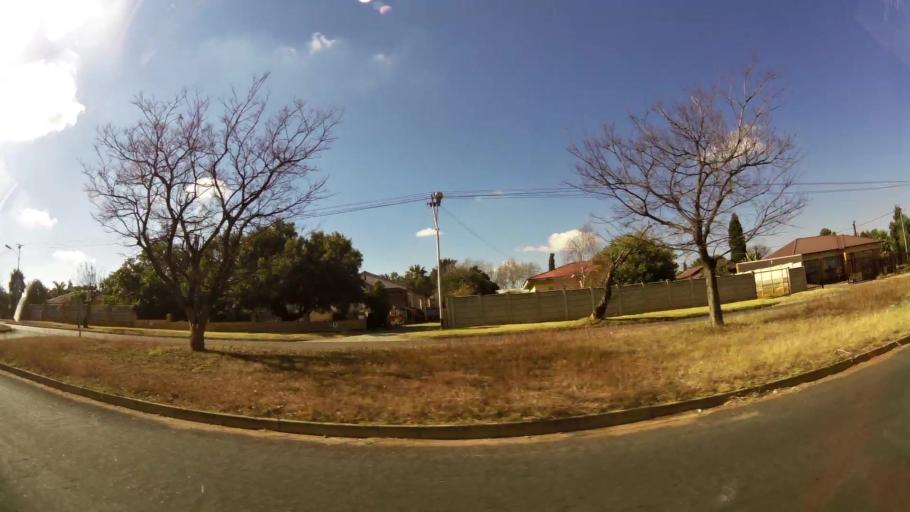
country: ZA
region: Gauteng
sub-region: City of Johannesburg Metropolitan Municipality
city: Roodepoort
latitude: -26.1315
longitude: 27.8326
